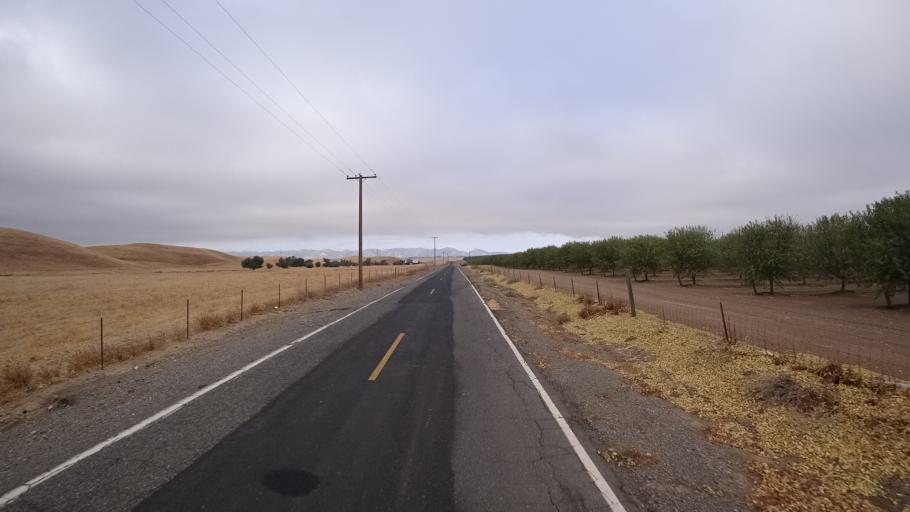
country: US
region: California
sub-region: Yolo County
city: Dunnigan
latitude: 38.8623
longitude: -122.0358
